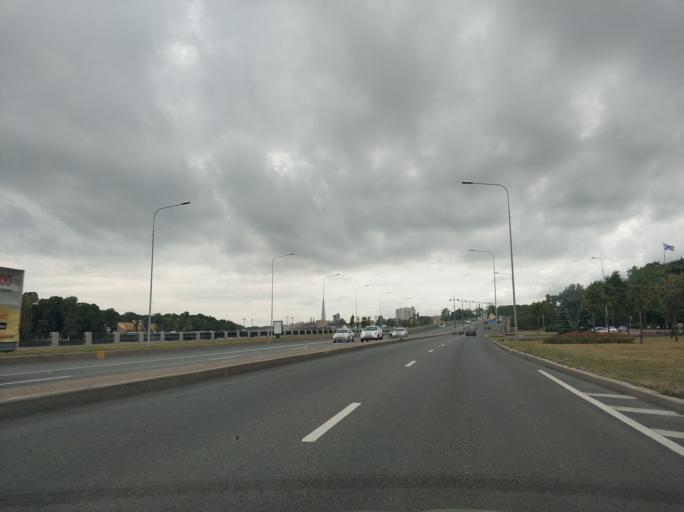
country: RU
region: Leningrad
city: Chernaya Rechka
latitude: 59.9825
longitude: 30.3073
